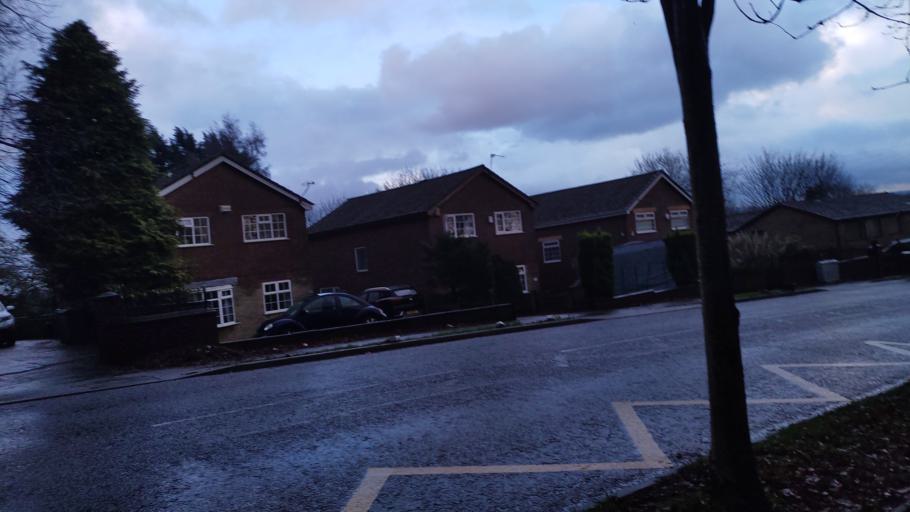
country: GB
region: England
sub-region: Blackburn with Darwen
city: Blackburn
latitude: 53.7435
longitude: -2.5084
